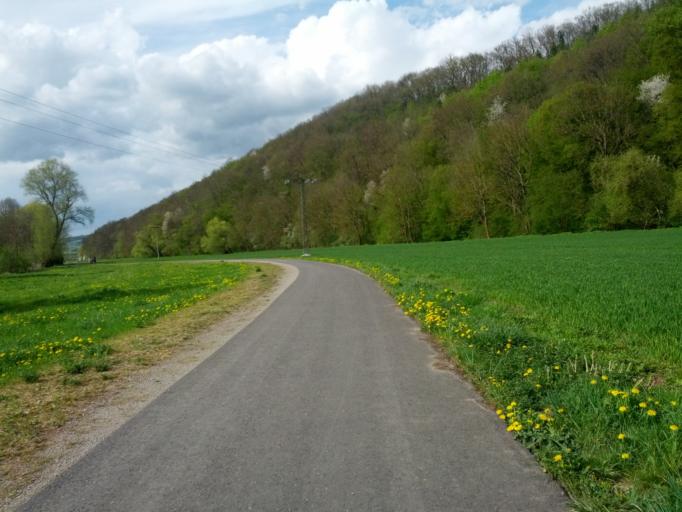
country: DE
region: Thuringia
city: Creuzburg
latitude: 51.0264
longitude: 10.2367
